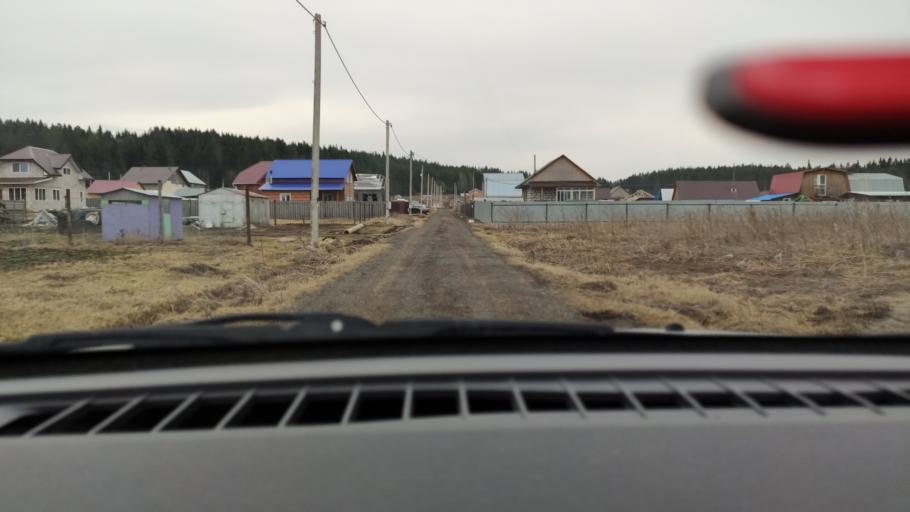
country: RU
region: Perm
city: Kultayevo
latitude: 57.8952
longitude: 56.0156
